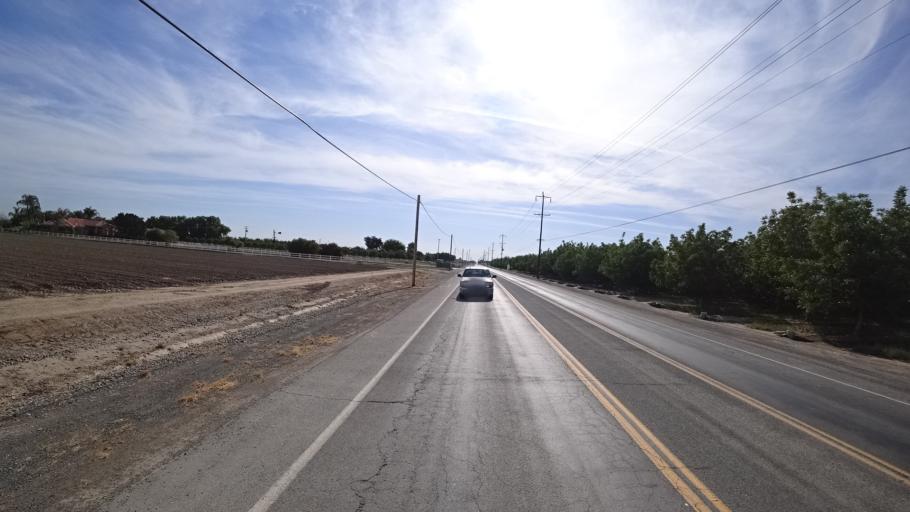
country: US
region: California
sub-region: Kings County
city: Hanford
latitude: 36.3426
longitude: -119.5984
